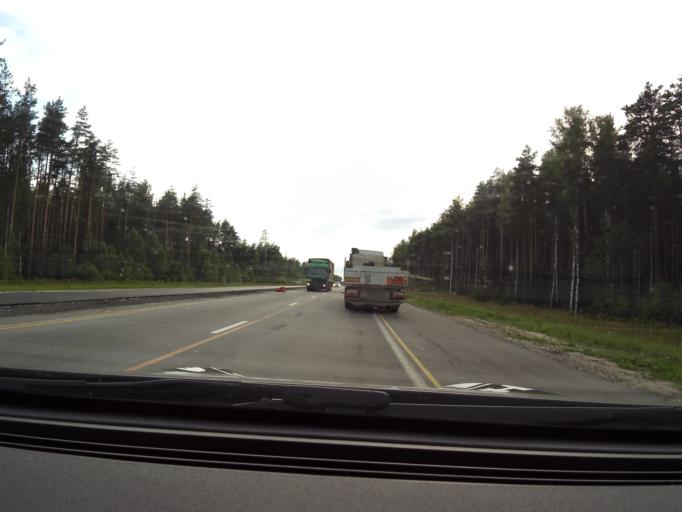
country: RU
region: Vladimir
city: Orgtrud
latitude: 56.1030
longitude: 40.7180
